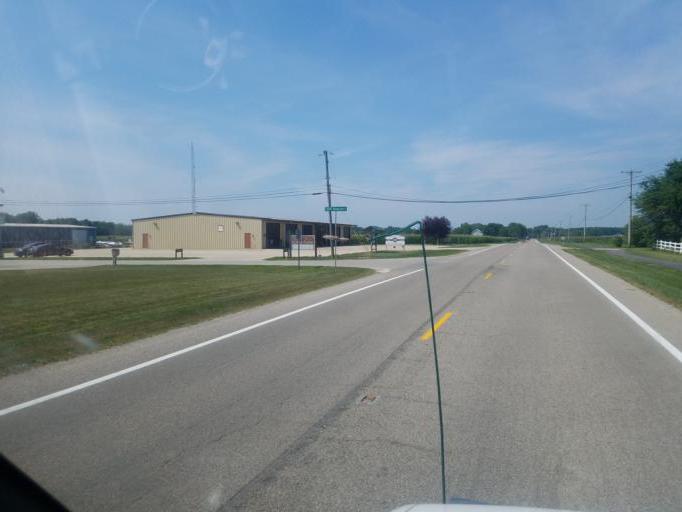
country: US
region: Ohio
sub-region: Mercer County
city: Celina
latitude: 40.4921
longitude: -84.5409
